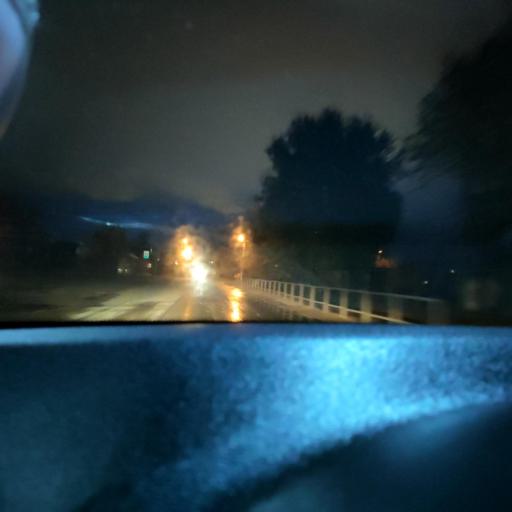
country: RU
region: Samara
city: Samara
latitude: 53.1834
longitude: 50.2425
